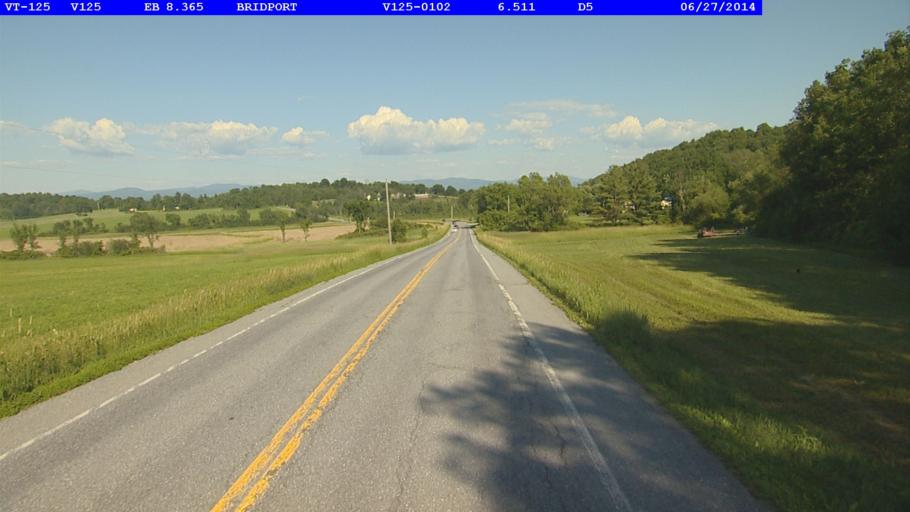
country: US
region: Vermont
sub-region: Addison County
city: Middlebury (village)
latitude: 43.9905
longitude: -73.2876
